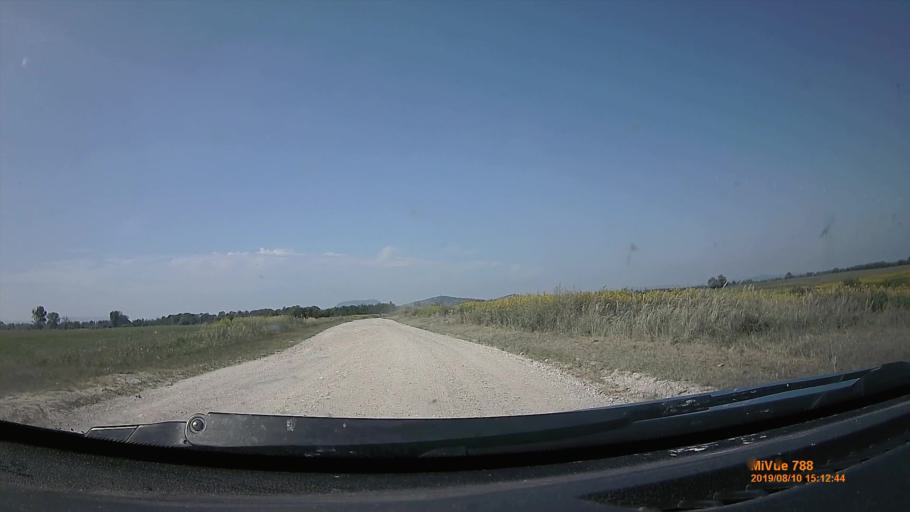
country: HU
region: Somogy
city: Fonyod
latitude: 46.6885
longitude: 17.5629
